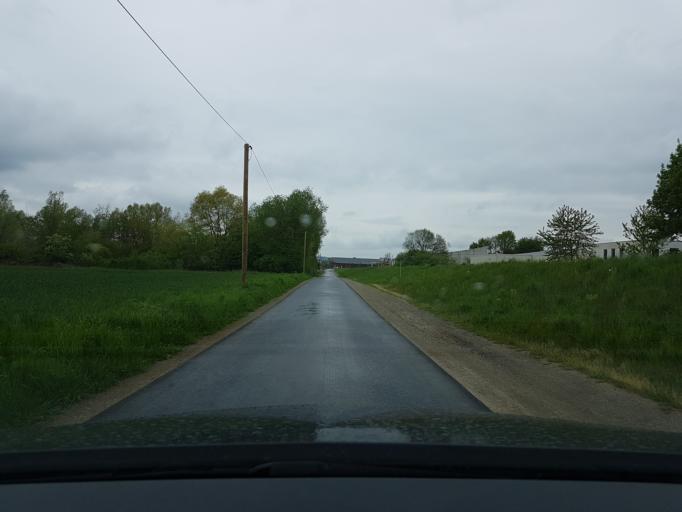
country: DE
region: Lower Saxony
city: Hameln
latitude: 52.0874
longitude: 9.3703
